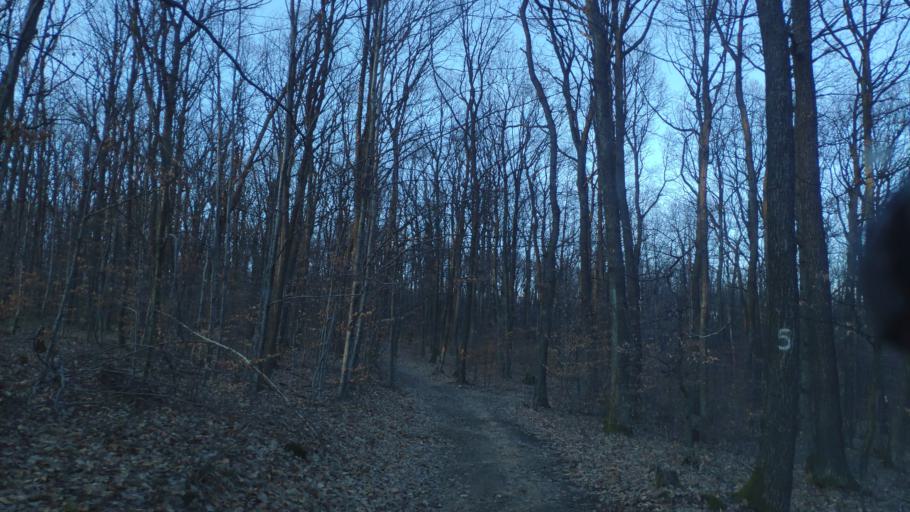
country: SK
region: Kosicky
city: Kosice
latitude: 48.6954
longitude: 21.1813
